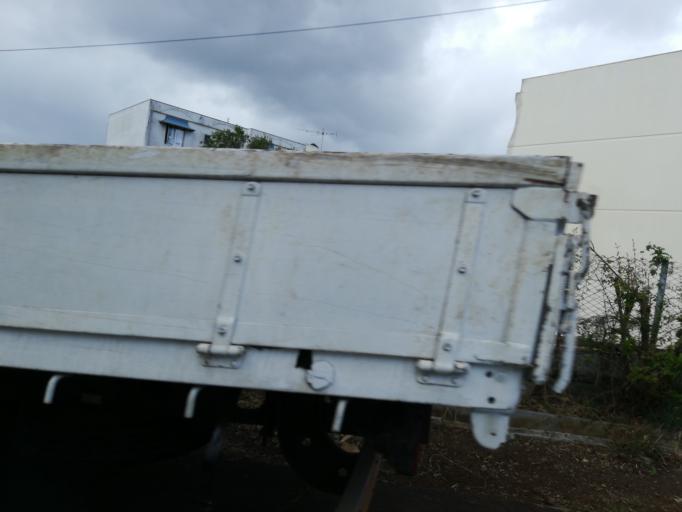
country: MU
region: Moka
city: Moka
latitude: -20.2148
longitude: 57.4756
